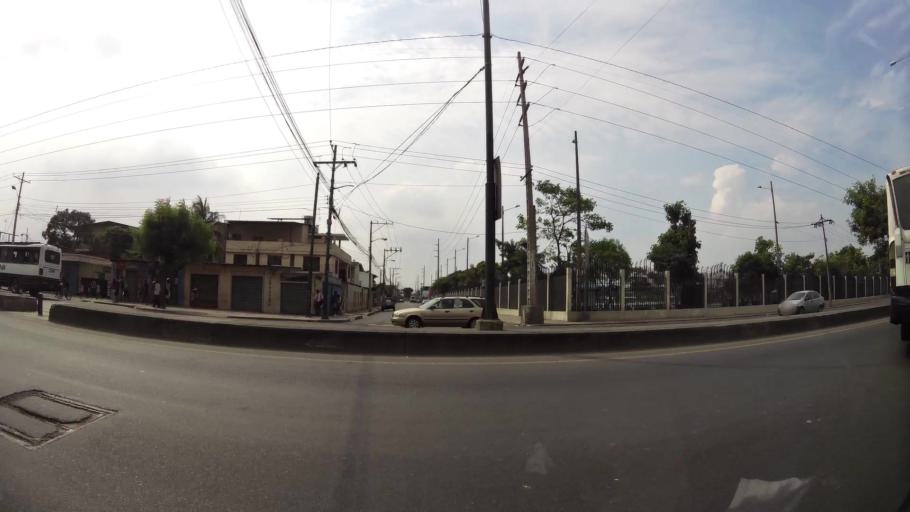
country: EC
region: Guayas
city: Guayaquil
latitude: -2.2390
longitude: -79.9013
